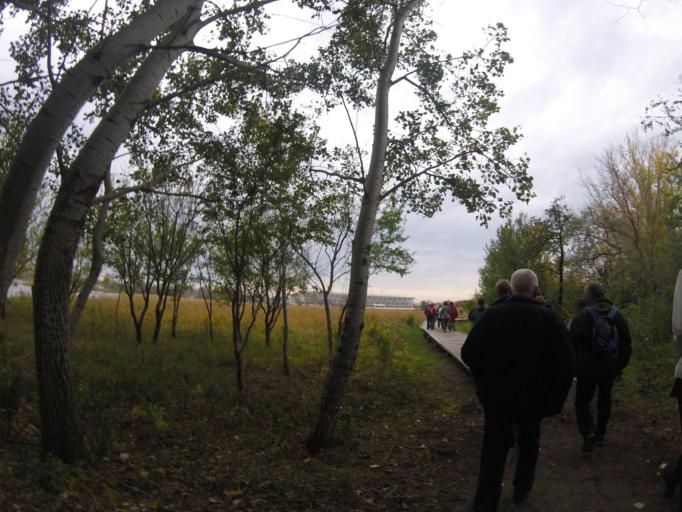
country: HU
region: Fejer
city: Szekesfehervar
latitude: 47.1711
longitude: 18.4202
